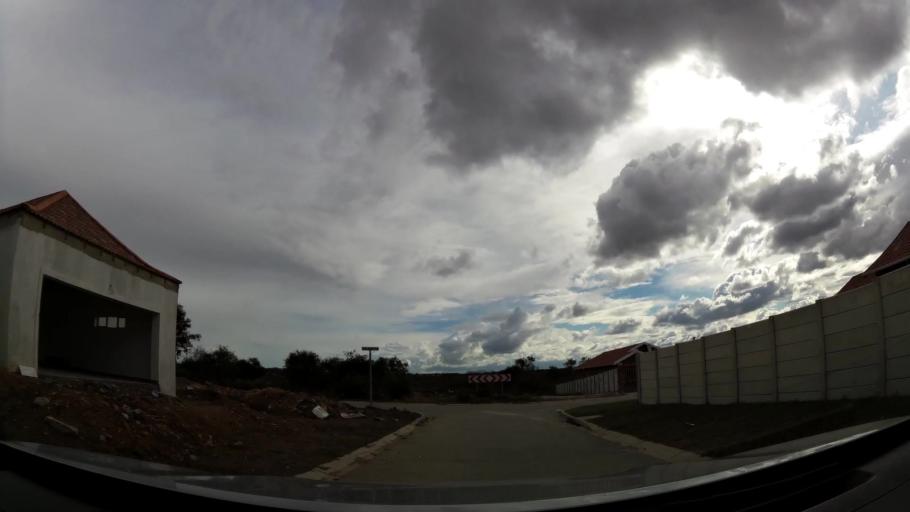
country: ZA
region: Eastern Cape
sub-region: Nelson Mandela Bay Metropolitan Municipality
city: Port Elizabeth
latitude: -33.9287
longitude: 25.5017
